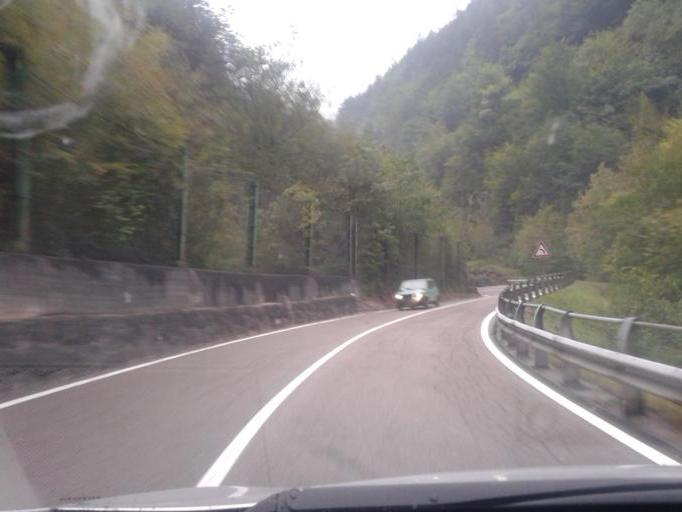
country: IT
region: Trentino-Alto Adige
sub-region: Provincia di Trento
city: Storo
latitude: 45.8452
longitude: 10.6082
